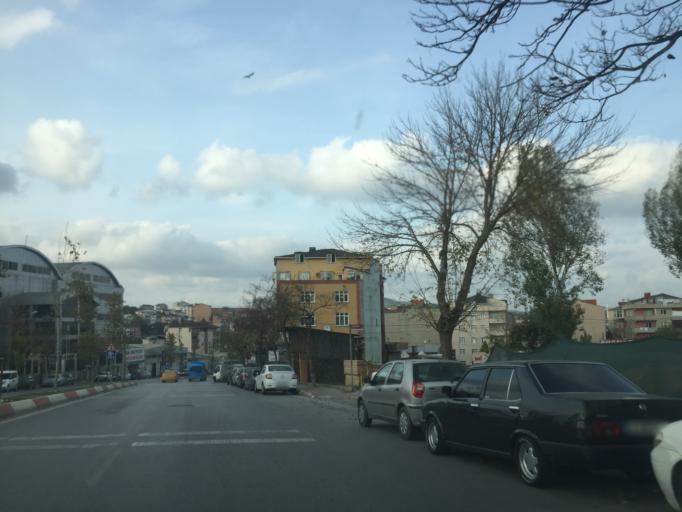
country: TR
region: Istanbul
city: Sultanbeyli
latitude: 40.9448
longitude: 29.3000
